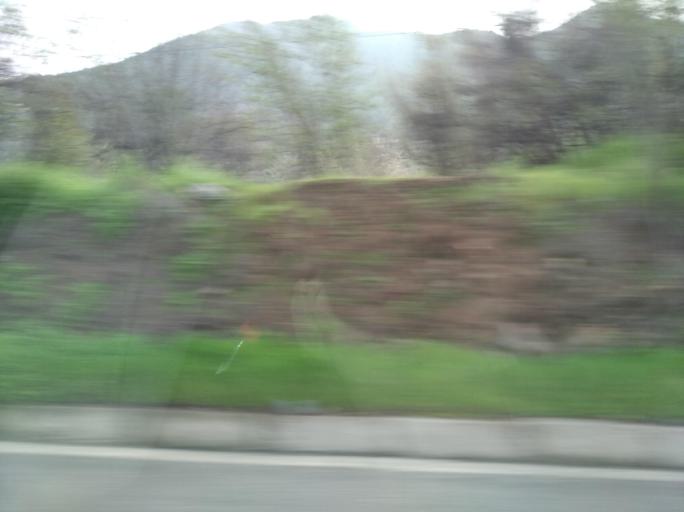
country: CL
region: Santiago Metropolitan
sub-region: Provincia de Chacabuco
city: Lampa
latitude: -33.0748
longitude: -70.9602
